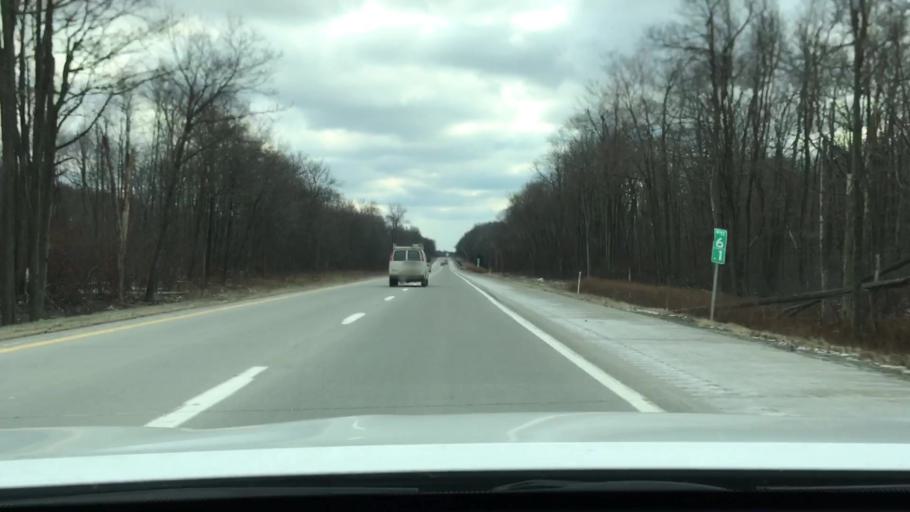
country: US
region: Pennsylvania
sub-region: Monroe County
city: Mount Pocono
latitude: 41.1549
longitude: -75.4134
